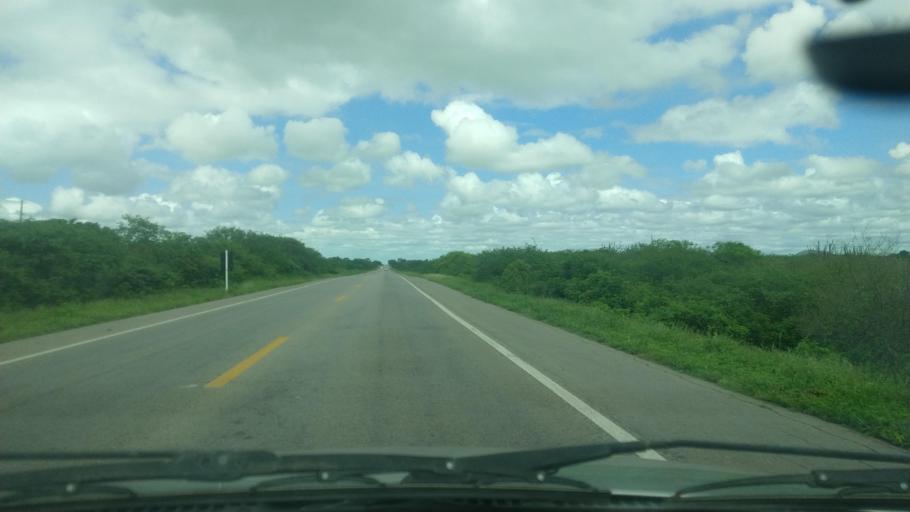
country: BR
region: Rio Grande do Norte
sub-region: Tangara
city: Tangara
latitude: -6.1643
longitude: -35.7562
